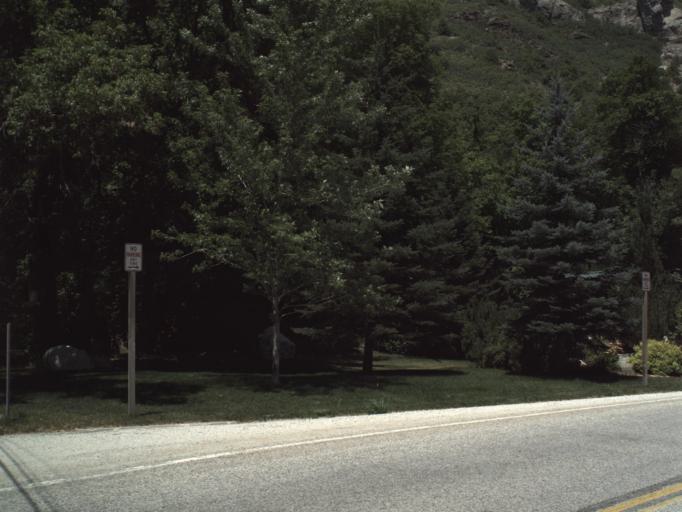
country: US
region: Utah
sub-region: Weber County
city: Liberty
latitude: 41.2488
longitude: -111.8855
